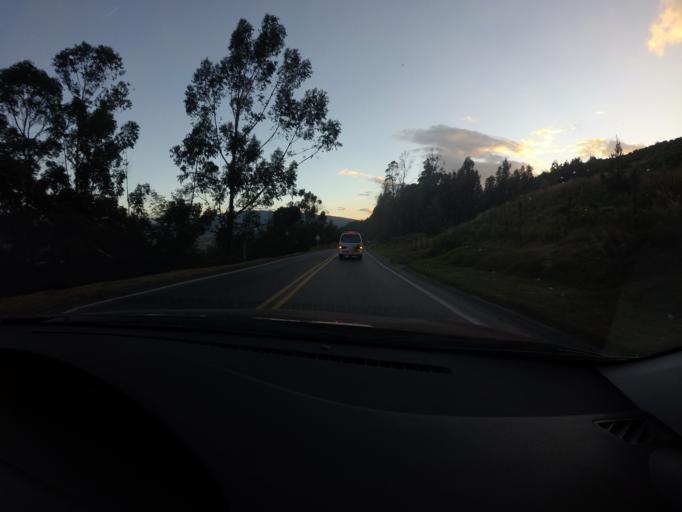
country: CO
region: Cundinamarca
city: Nemocon
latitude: 5.1227
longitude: -73.9065
